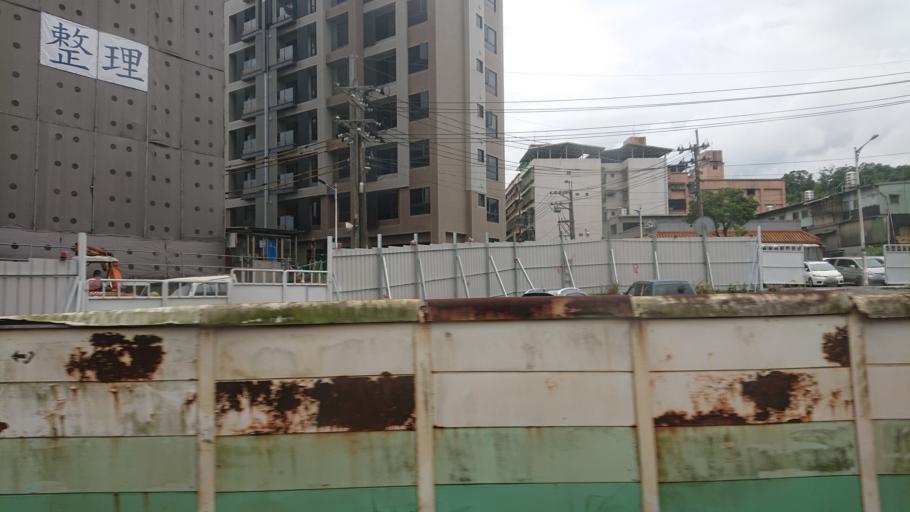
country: TW
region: Taiwan
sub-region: Keelung
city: Keelung
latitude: 25.0892
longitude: 121.7073
